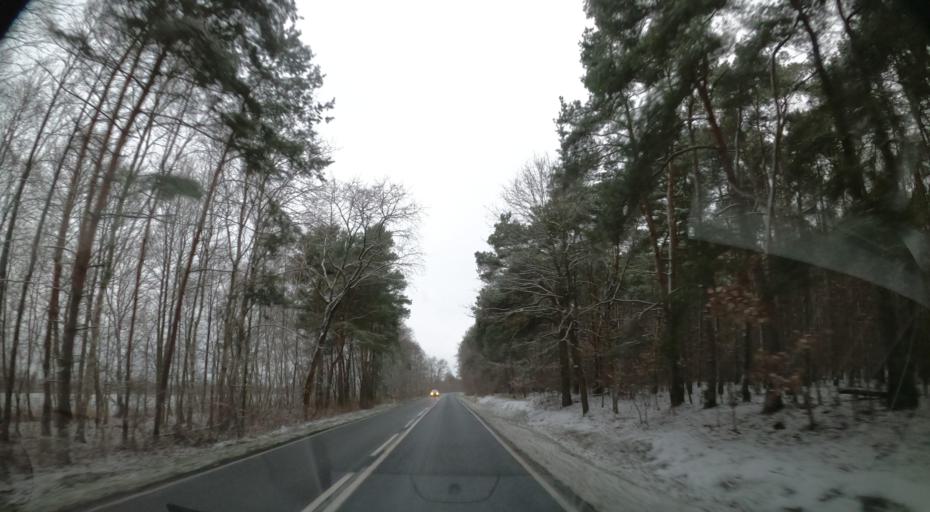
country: PL
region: Masovian Voivodeship
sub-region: Powiat plocki
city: Maszewo Duze
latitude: 52.5746
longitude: 19.5545
